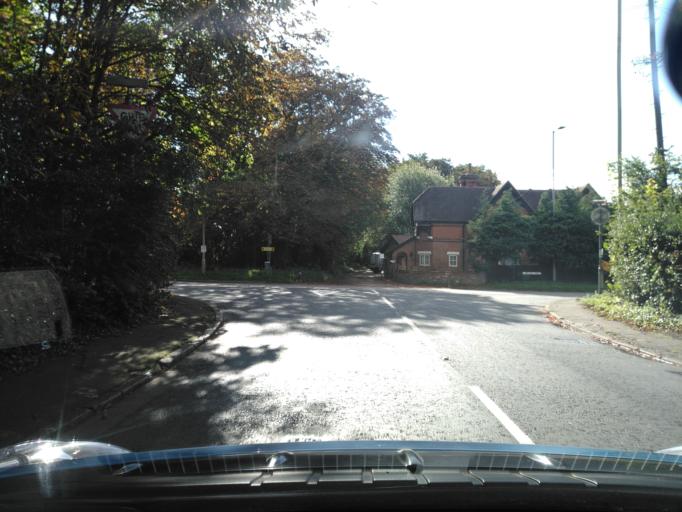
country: GB
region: England
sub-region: Hertfordshire
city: Elstree
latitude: 51.6492
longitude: -0.2969
